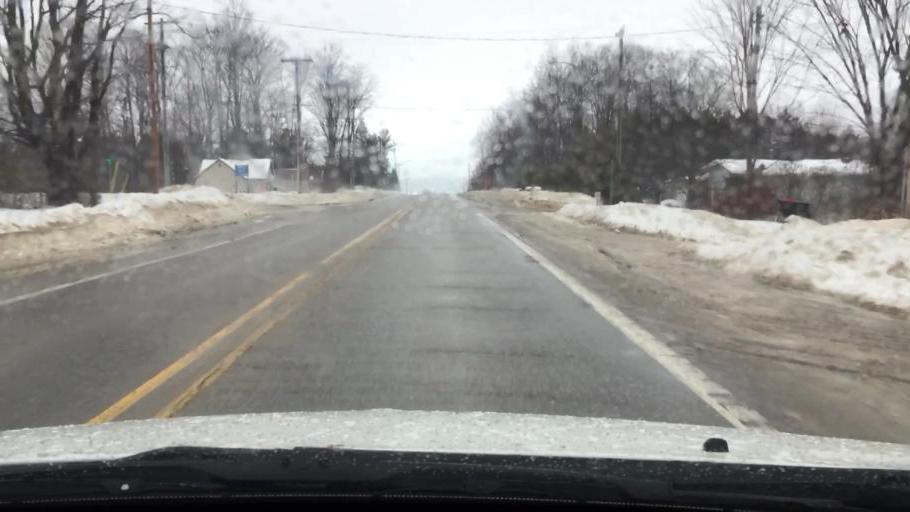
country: US
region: Michigan
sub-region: Charlevoix County
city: East Jordan
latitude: 45.1466
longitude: -85.1398
